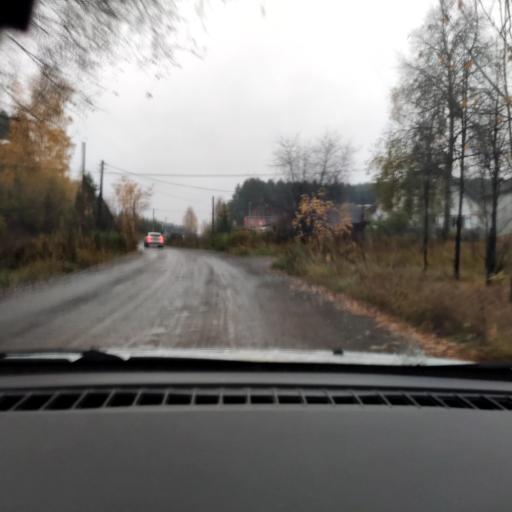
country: RU
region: Perm
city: Kondratovo
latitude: 58.0477
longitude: 56.1037
